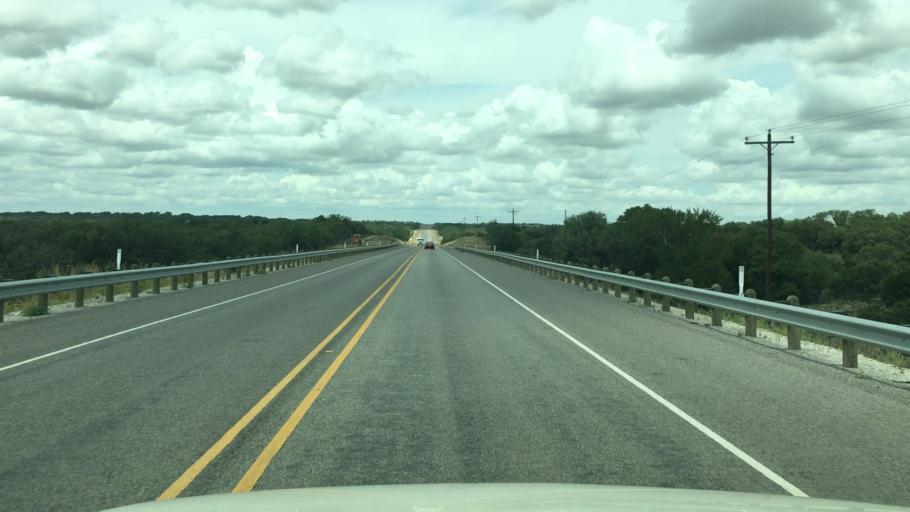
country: US
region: Texas
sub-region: McCulloch County
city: Brady
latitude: 31.0361
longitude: -99.2370
